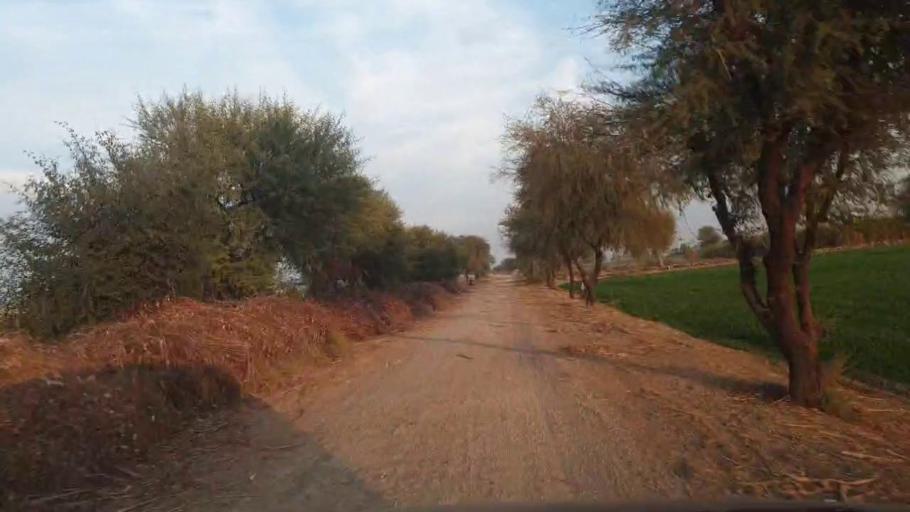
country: PK
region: Sindh
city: Shahpur Chakar
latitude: 26.0528
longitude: 68.5393
